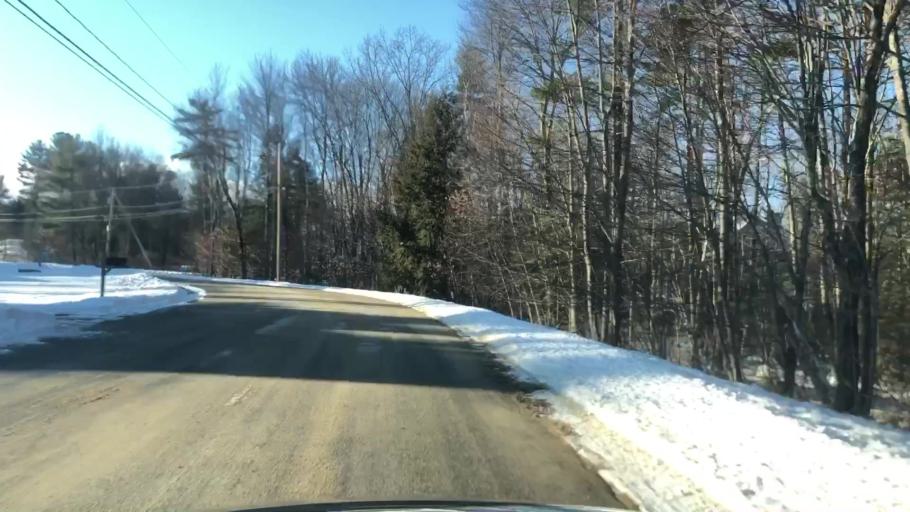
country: US
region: New Hampshire
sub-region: Hillsborough County
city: Milford
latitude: 42.7957
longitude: -71.6662
